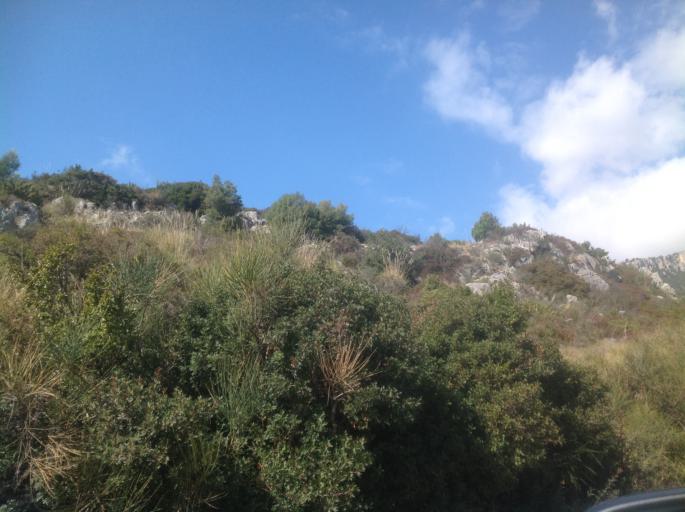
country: IT
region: Calabria
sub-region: Provincia di Cosenza
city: Civita
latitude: 39.8235
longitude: 16.3098
